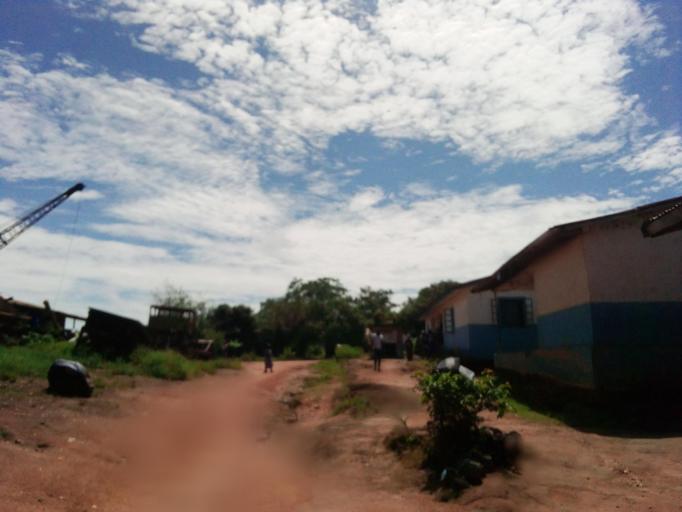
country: SL
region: Eastern Province
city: Koidu
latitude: 8.6670
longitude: -10.9459
